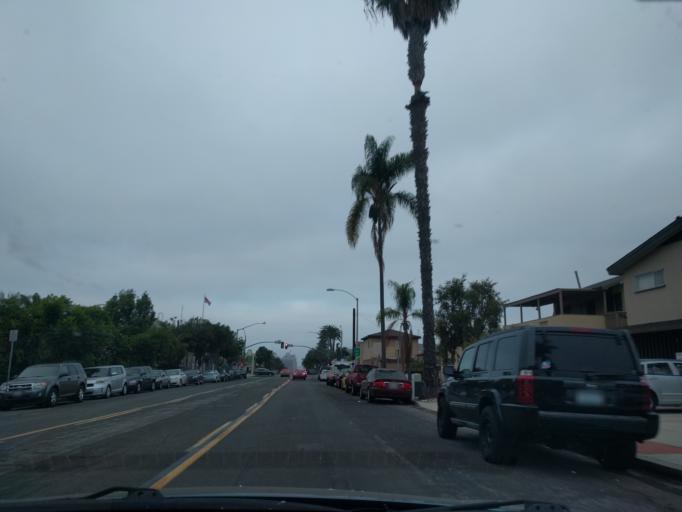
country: US
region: California
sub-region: San Diego County
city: San Diego
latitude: 32.7159
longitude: -117.1390
